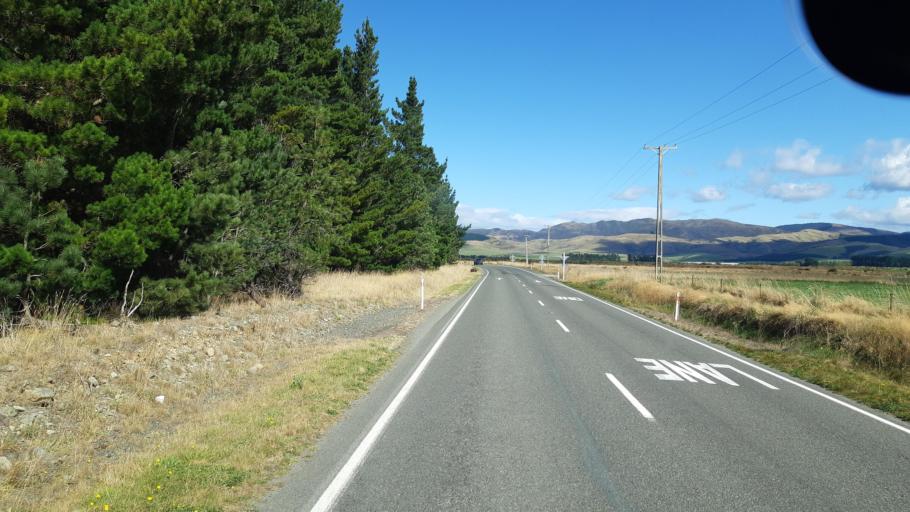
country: NZ
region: Southland
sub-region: Southland District
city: Winton
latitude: -45.7836
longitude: 168.1730
